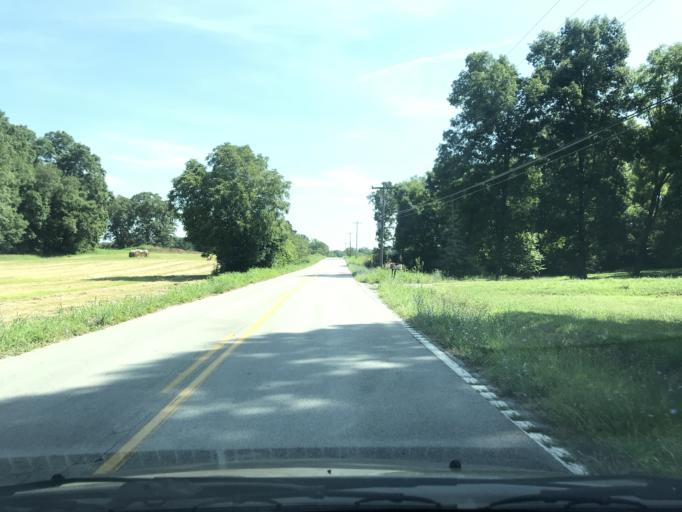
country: US
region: Tennessee
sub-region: Hamilton County
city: Lakesite
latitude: 35.2830
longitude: -85.0528
